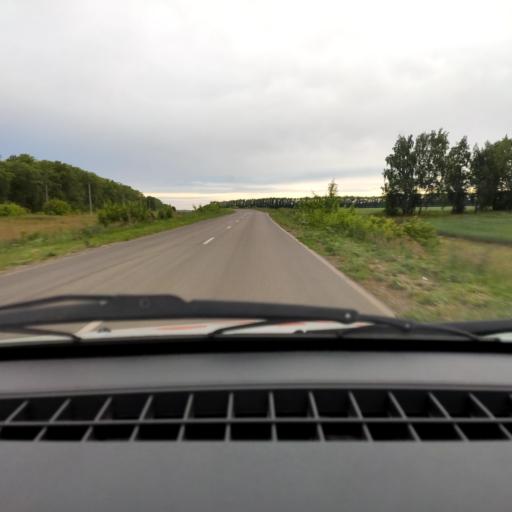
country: RU
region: Bashkortostan
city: Avdon
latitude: 54.5175
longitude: 55.7727
